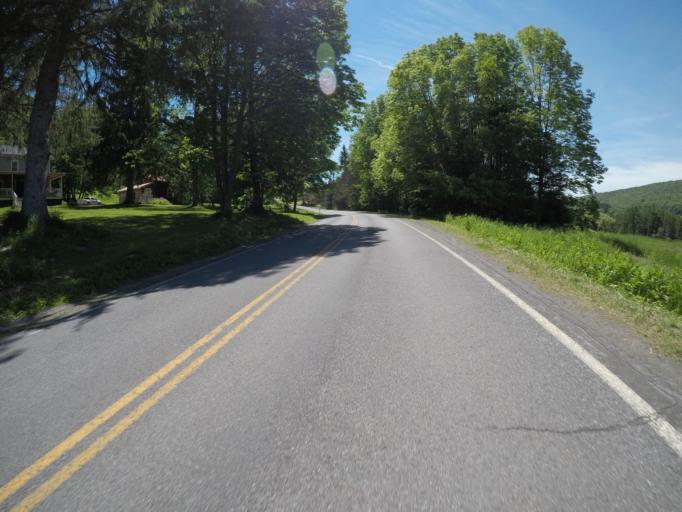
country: US
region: New York
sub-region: Delaware County
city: Delhi
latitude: 42.1901
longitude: -74.8057
